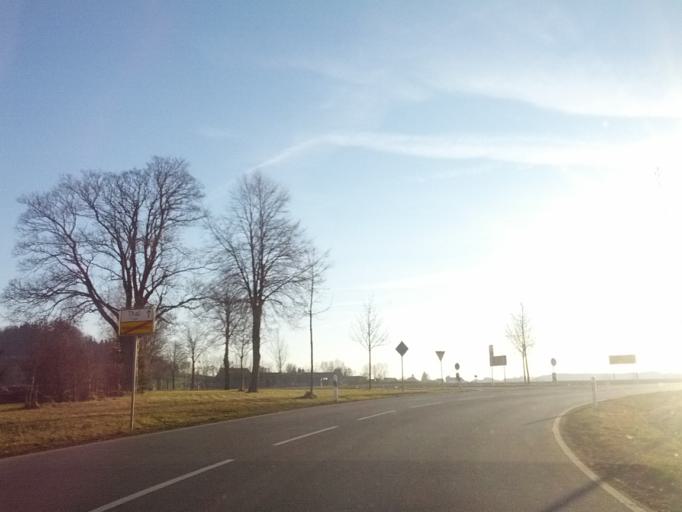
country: DE
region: Bavaria
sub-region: Swabia
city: Wolfertschwenden
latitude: 47.8893
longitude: 10.2714
